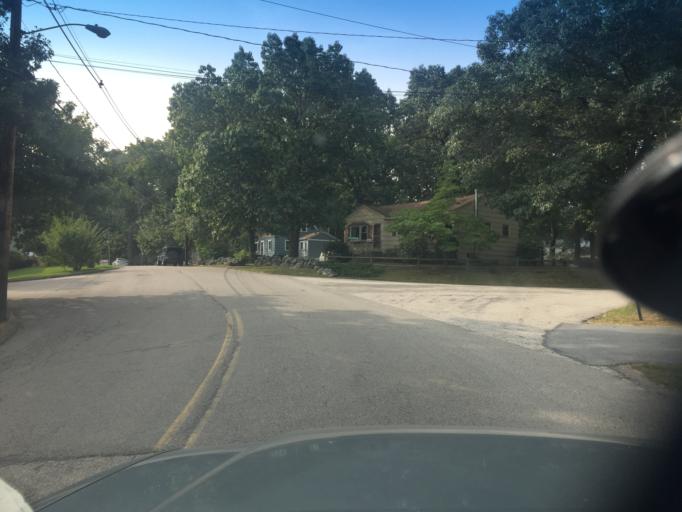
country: US
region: Massachusetts
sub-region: Norfolk County
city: Bellingham
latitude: 42.1233
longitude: -71.4752
